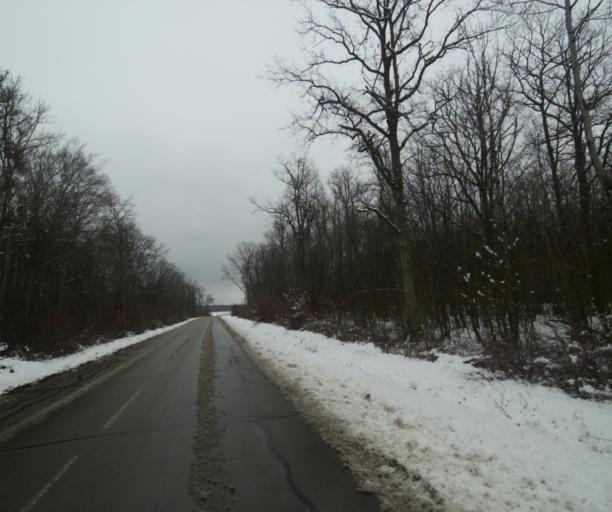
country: FR
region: Champagne-Ardenne
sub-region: Departement de la Haute-Marne
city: Laneuville-a-Remy
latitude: 48.4275
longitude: 4.8487
